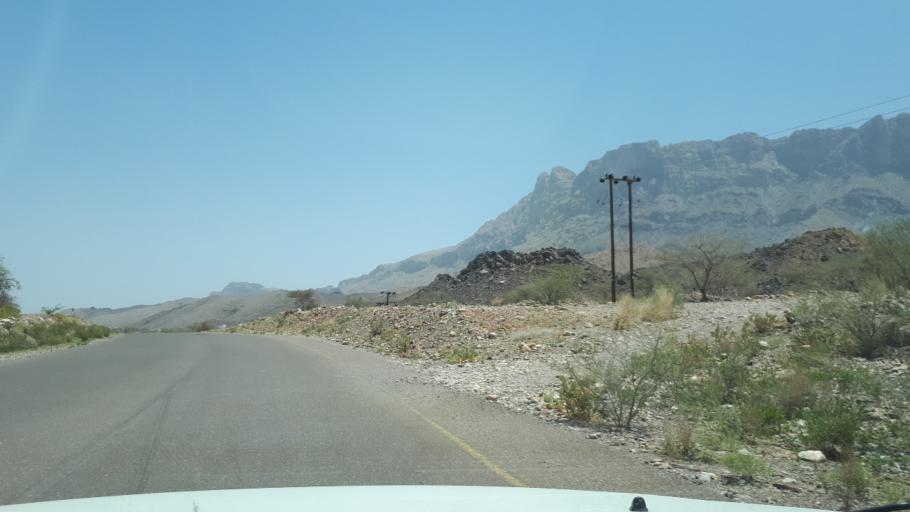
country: OM
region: Muhafazat ad Dakhiliyah
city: Bahla'
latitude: 23.1631
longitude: 57.1637
